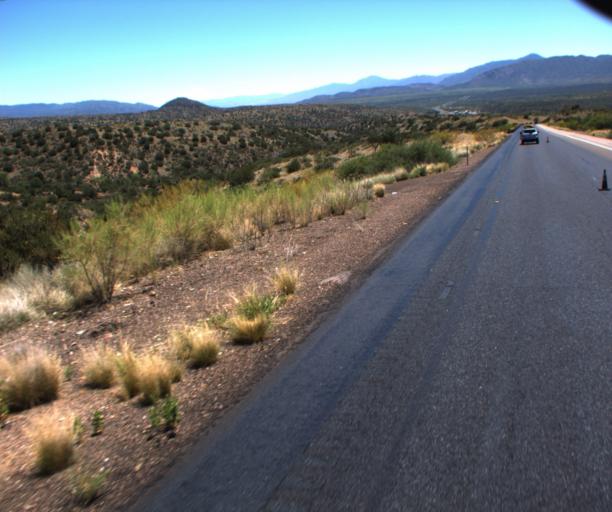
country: US
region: Arizona
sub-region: Gila County
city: Payson
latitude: 34.1446
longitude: -111.3505
